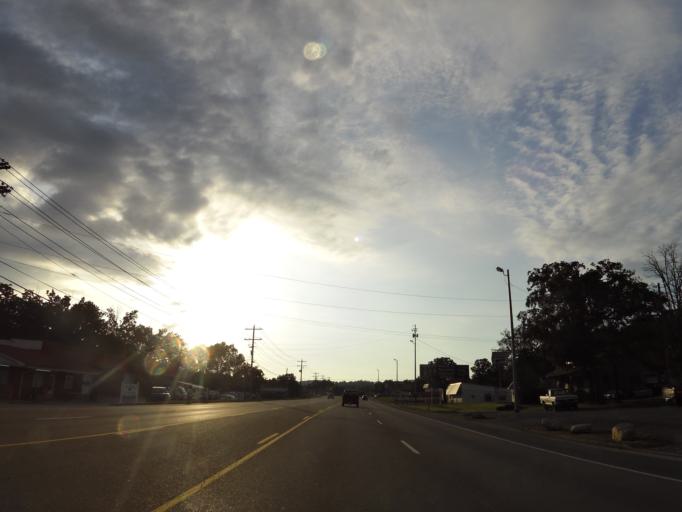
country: US
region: Tennessee
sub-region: Cocke County
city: Newport
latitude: 35.9730
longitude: -83.2144
